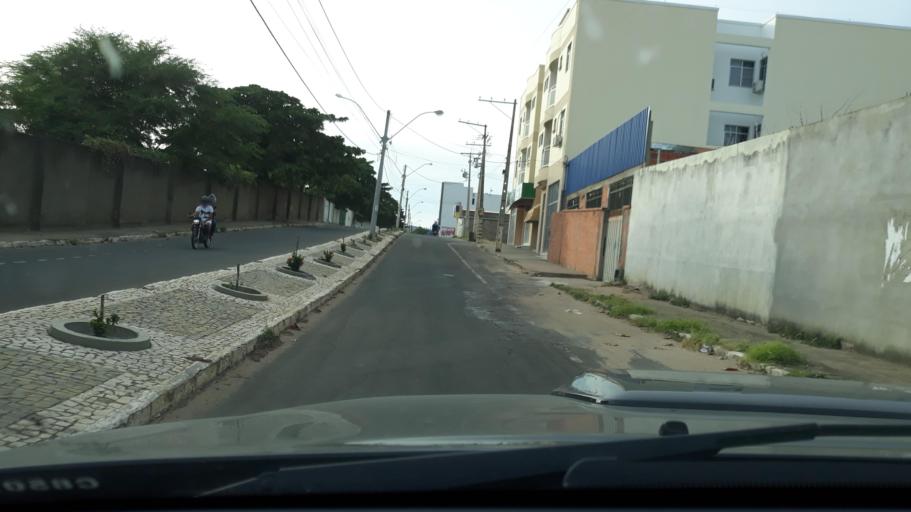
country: BR
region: Bahia
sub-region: Guanambi
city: Guanambi
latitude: -14.2352
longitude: -42.7712
